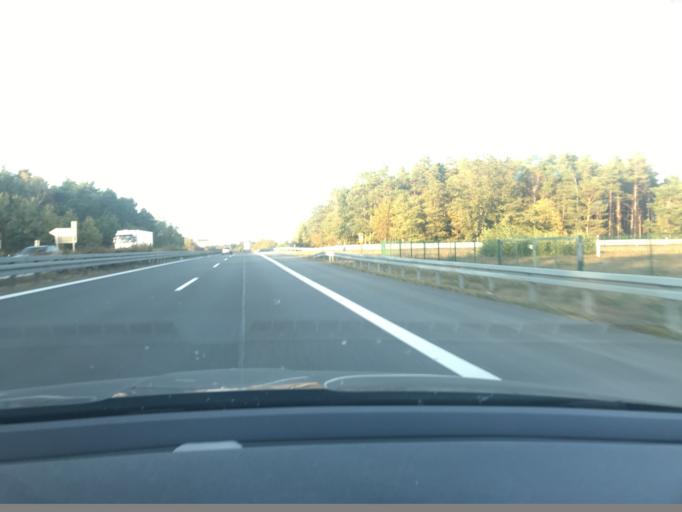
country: DE
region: Brandenburg
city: Schipkau
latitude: 51.5339
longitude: 13.9079
